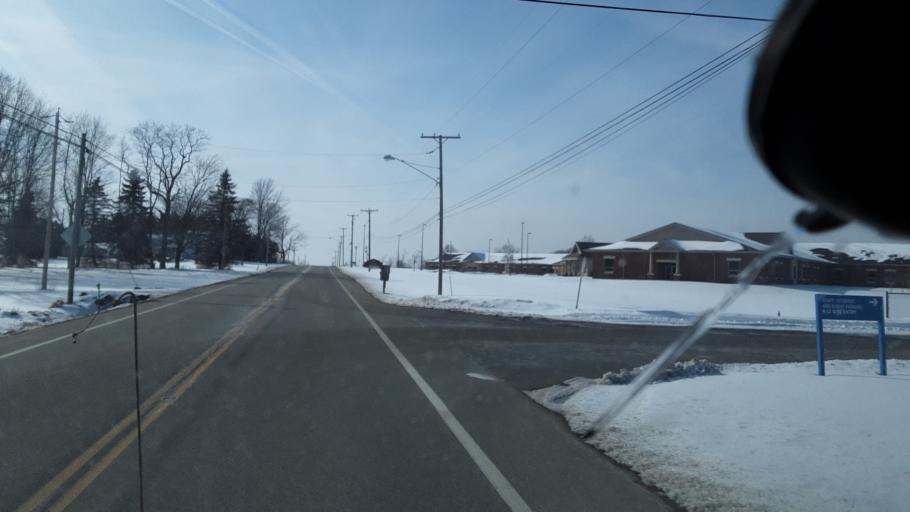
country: US
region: Ohio
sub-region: Mahoning County
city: Craig Beach
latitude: 41.0246
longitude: -80.9106
